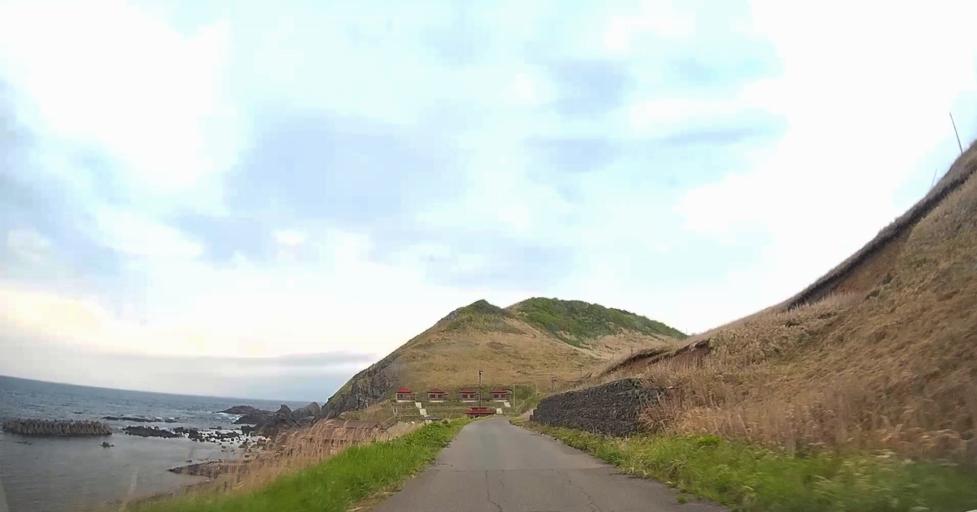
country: JP
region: Aomori
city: Shimokizukuri
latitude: 41.2516
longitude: 140.3432
